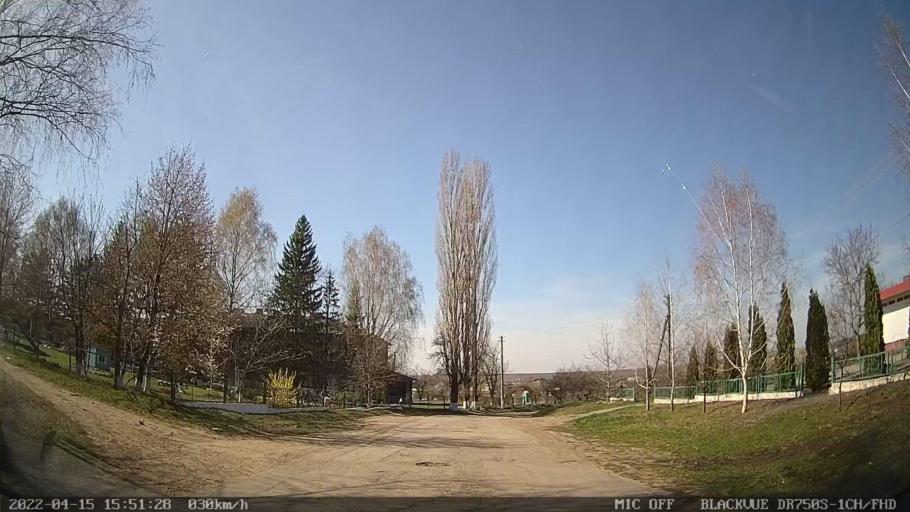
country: MD
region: Raionul Ocnita
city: Otaci
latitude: 48.3944
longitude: 27.8980
